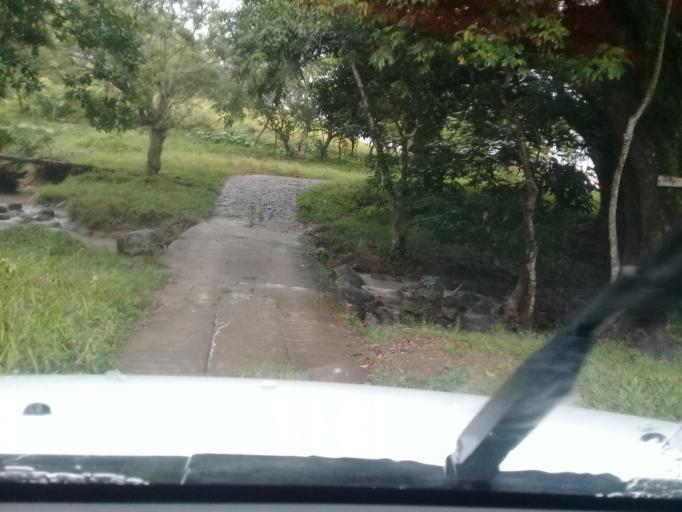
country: MX
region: Veracruz
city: Santiago Tuxtla
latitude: 18.4616
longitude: -95.3245
